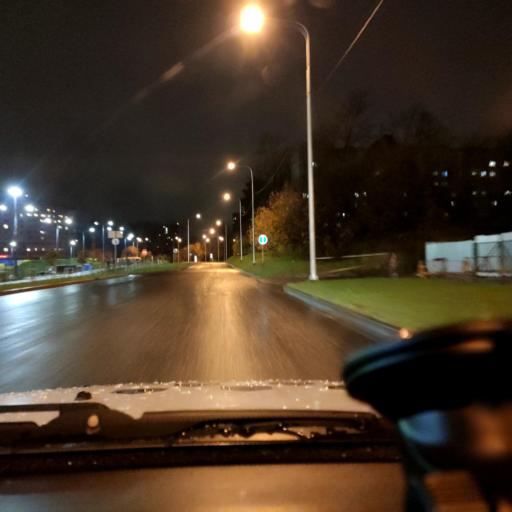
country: RU
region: Perm
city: Kondratovo
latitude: 57.9953
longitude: 56.1754
